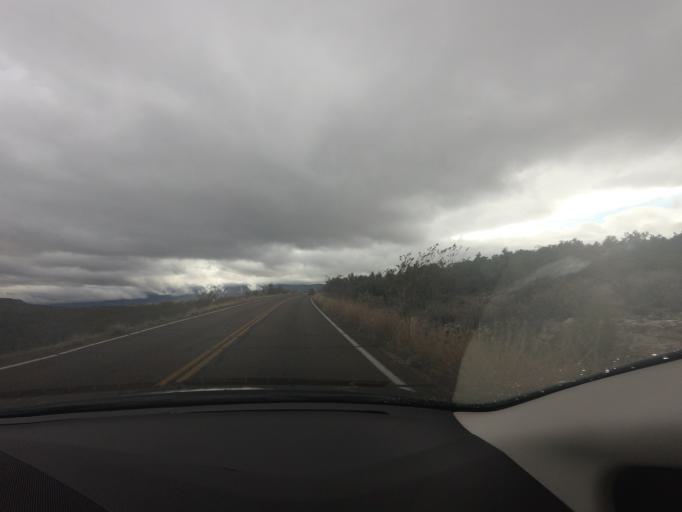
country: US
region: Arizona
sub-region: Yavapai County
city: Camp Verde
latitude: 34.6084
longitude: -111.8522
